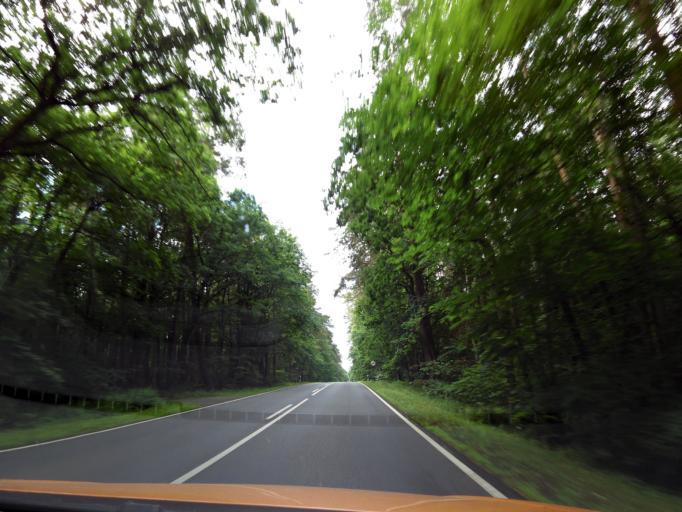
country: DE
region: Mecklenburg-Vorpommern
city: Krakow am See
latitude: 53.6263
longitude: 12.2538
